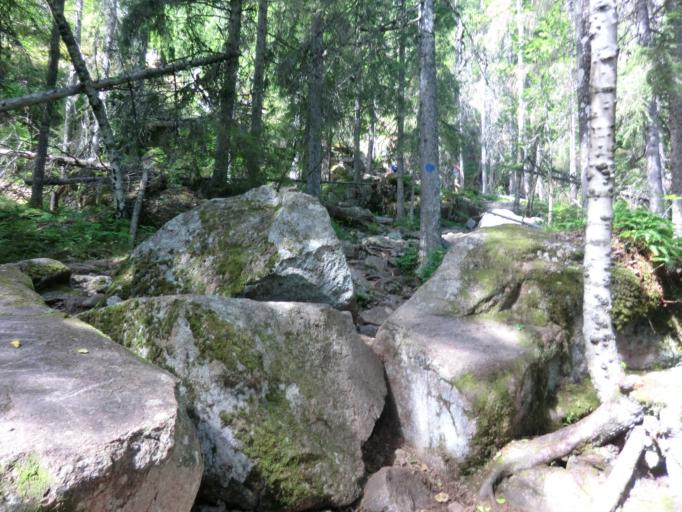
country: SE
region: Vaesternorrland
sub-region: Kramfors Kommun
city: Nordingra
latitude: 63.0729
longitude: 18.3515
